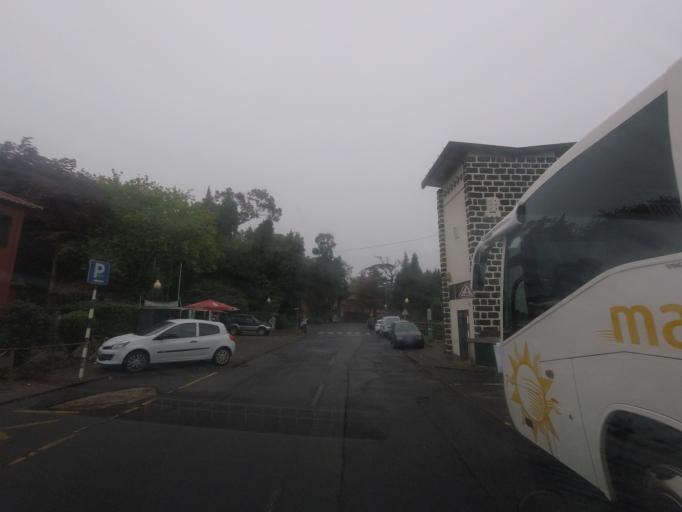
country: PT
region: Madeira
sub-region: Santa Cruz
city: Santa Cruz
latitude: 32.7241
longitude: -16.8187
